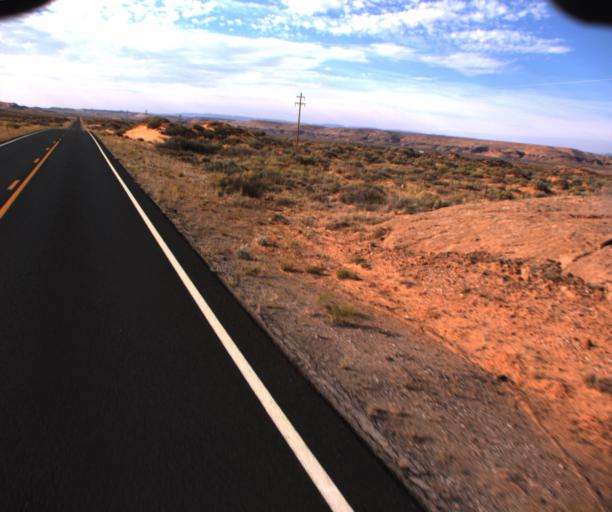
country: US
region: Arizona
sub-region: Apache County
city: Many Farms
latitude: 36.8143
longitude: -109.6465
